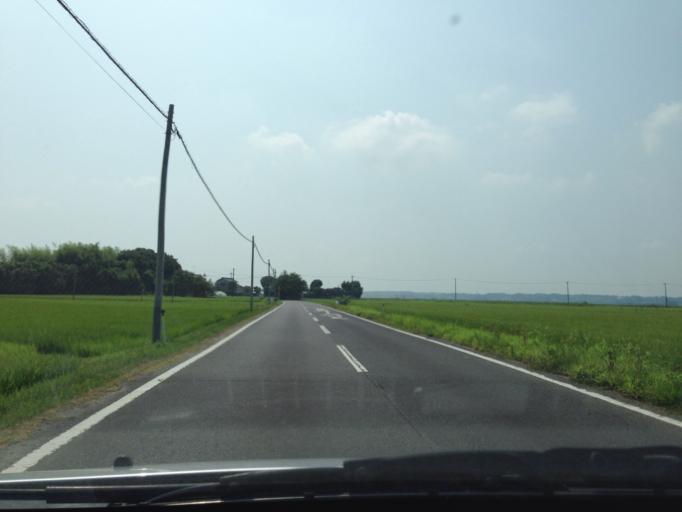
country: JP
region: Ibaraki
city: Inashiki
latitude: 36.0047
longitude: 140.3678
